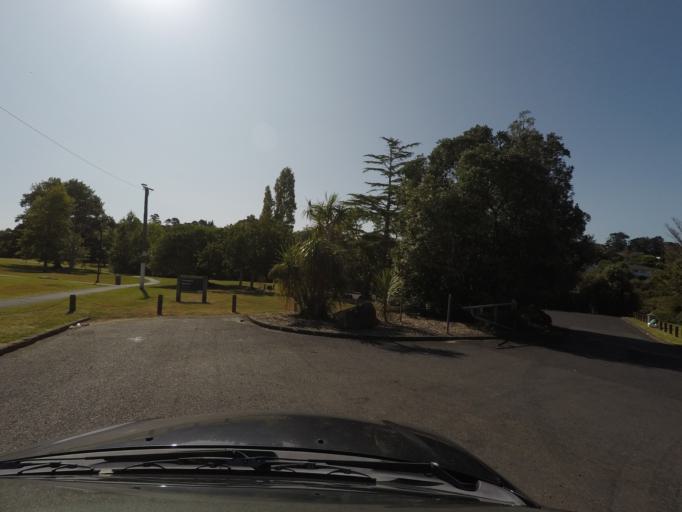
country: NZ
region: Auckland
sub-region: Auckland
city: Rosebank
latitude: -36.8557
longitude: 174.6187
